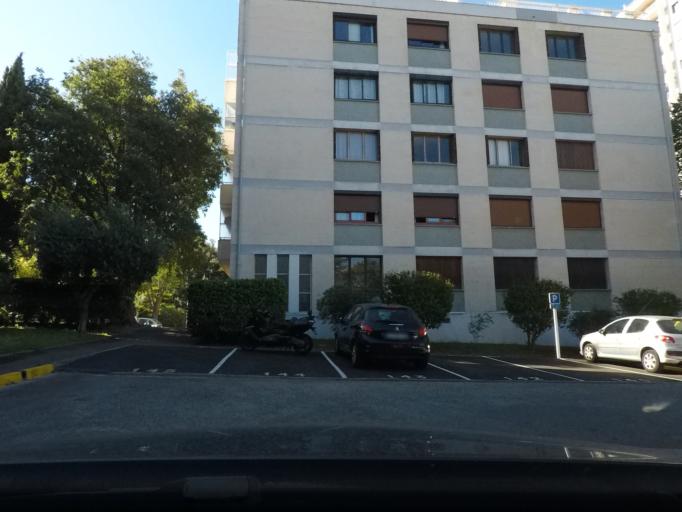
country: FR
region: Provence-Alpes-Cote d'Azur
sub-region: Departement des Bouches-du-Rhone
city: Marseille 09
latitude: 43.2556
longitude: 5.4176
